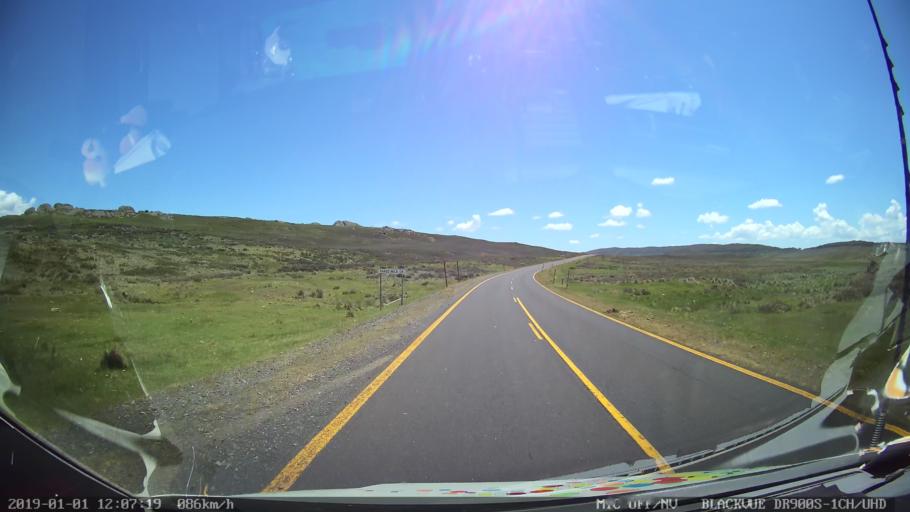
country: AU
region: New South Wales
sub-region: Tumut Shire
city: Tumut
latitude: -35.8345
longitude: 148.4895
